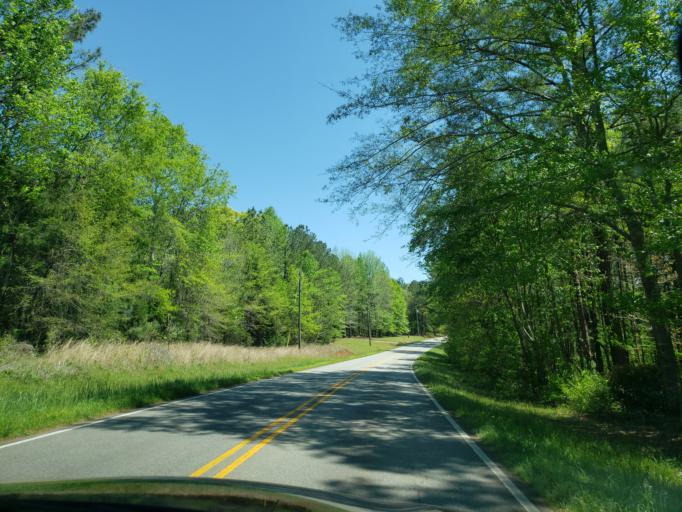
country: US
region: Alabama
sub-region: Tallapoosa County
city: Camp Hill
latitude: 32.7022
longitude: -85.7113
